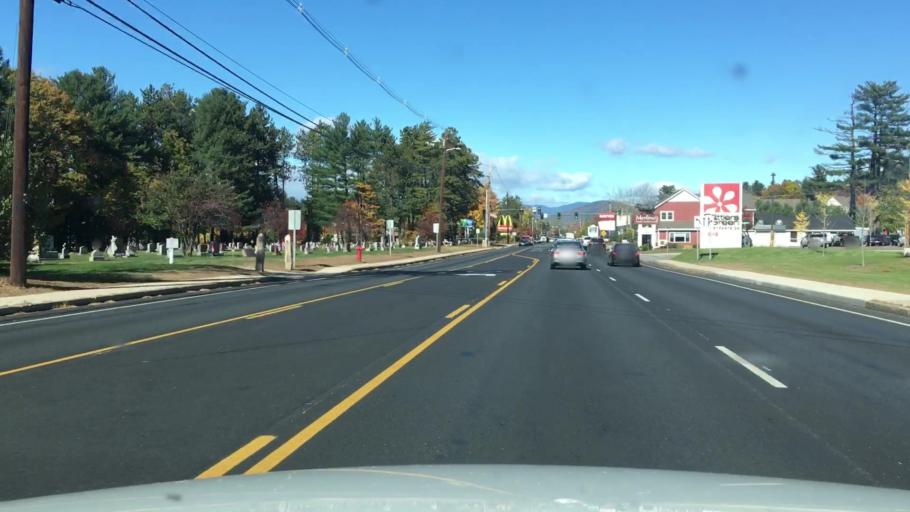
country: US
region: New Hampshire
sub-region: Carroll County
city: North Conway
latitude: 44.0251
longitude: -71.1178
